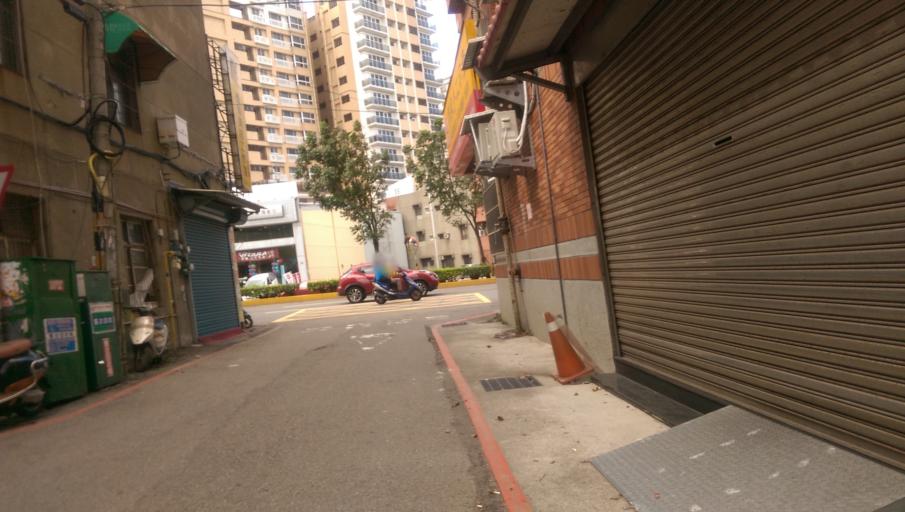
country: TW
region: Taiwan
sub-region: Hsinchu
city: Hsinchu
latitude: 24.7985
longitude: 120.9535
